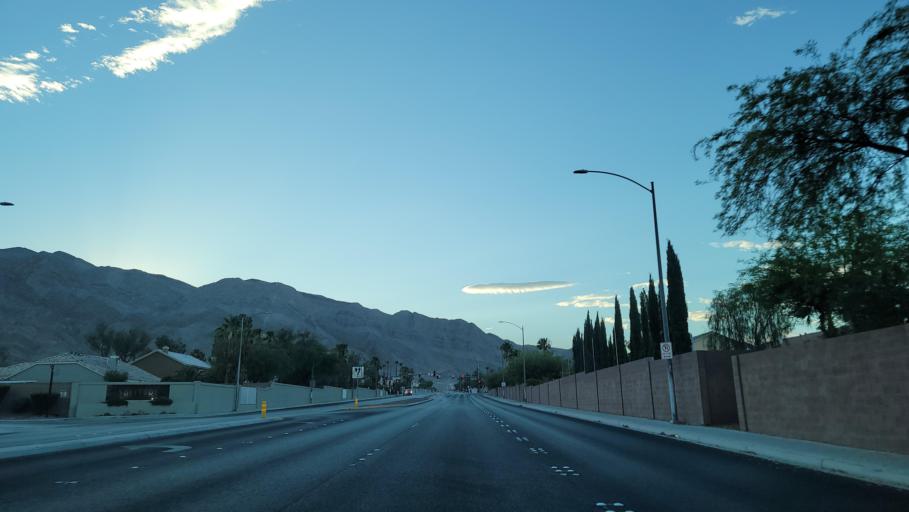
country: US
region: Nevada
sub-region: Clark County
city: Sunrise Manor
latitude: 36.1592
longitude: -115.0286
